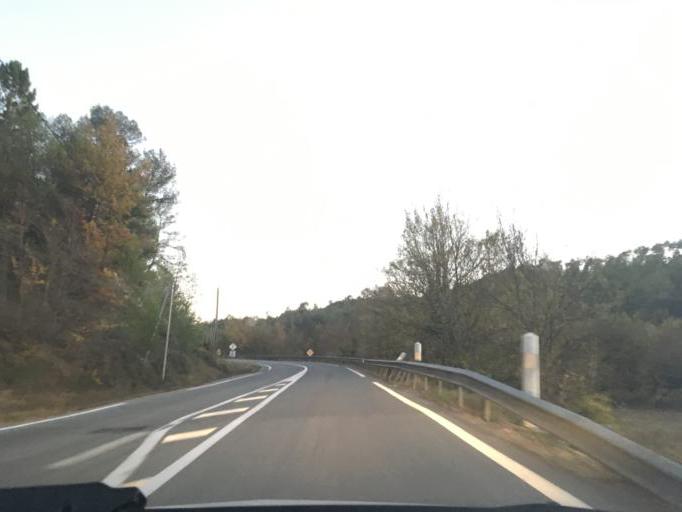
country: FR
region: Provence-Alpes-Cote d'Azur
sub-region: Departement du Var
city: Montferrat
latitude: 43.5953
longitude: 6.4682
